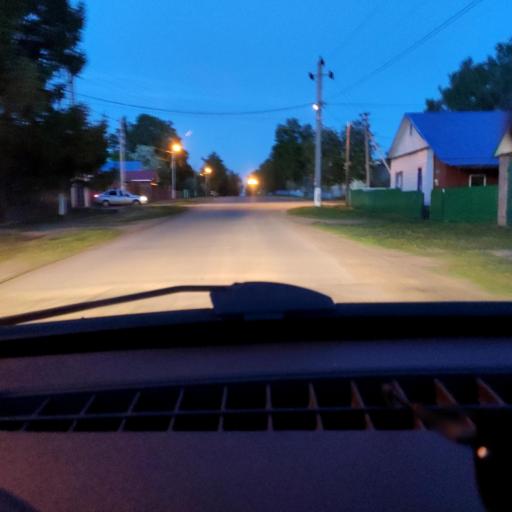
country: RU
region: Bashkortostan
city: Karmaskaly
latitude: 54.3704
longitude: 56.1669
